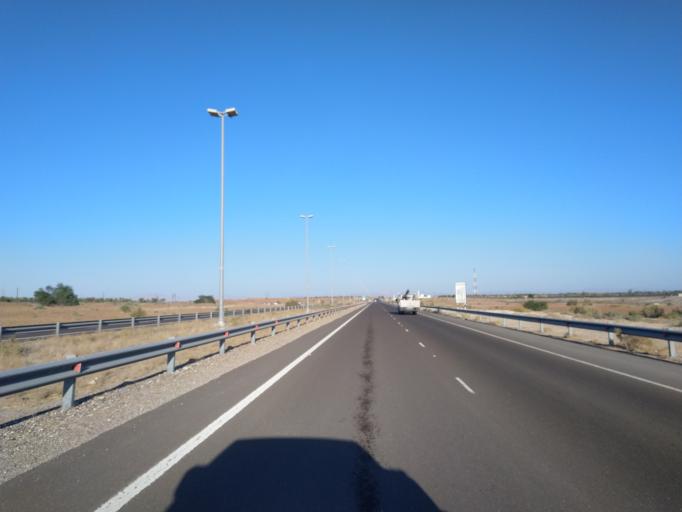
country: OM
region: Al Buraimi
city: Al Buraymi
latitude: 24.5397
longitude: 55.6212
